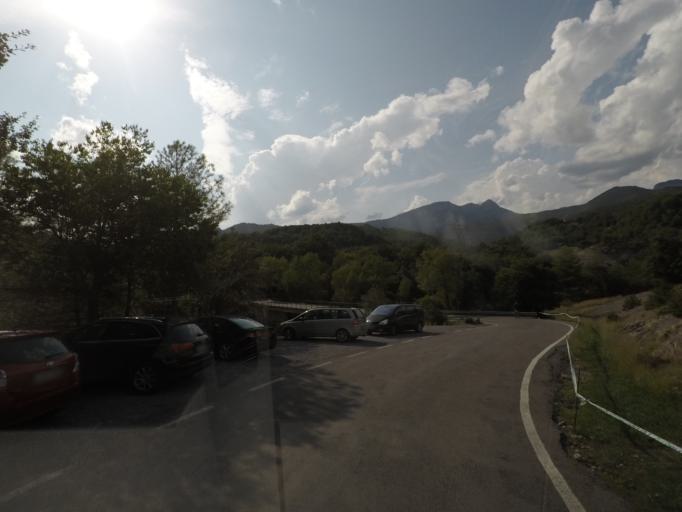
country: ES
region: Aragon
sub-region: Provincia de Huesca
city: Laspuna
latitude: 42.5091
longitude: 0.1274
